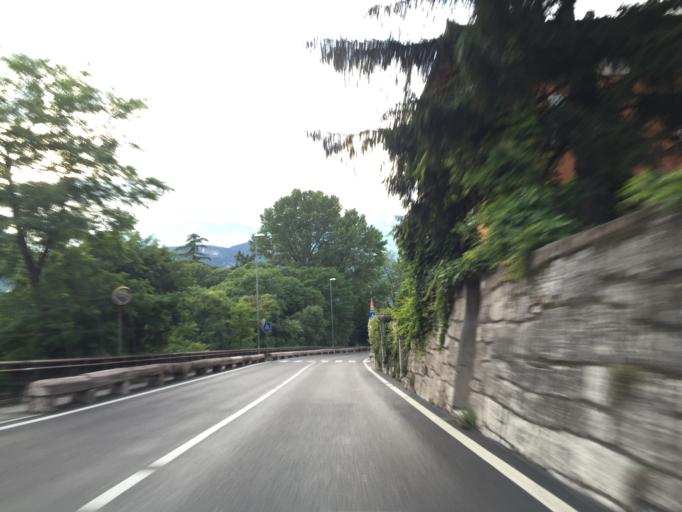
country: IT
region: Trentino-Alto Adige
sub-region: Provincia di Trento
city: Trento
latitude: 46.0674
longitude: 11.1302
